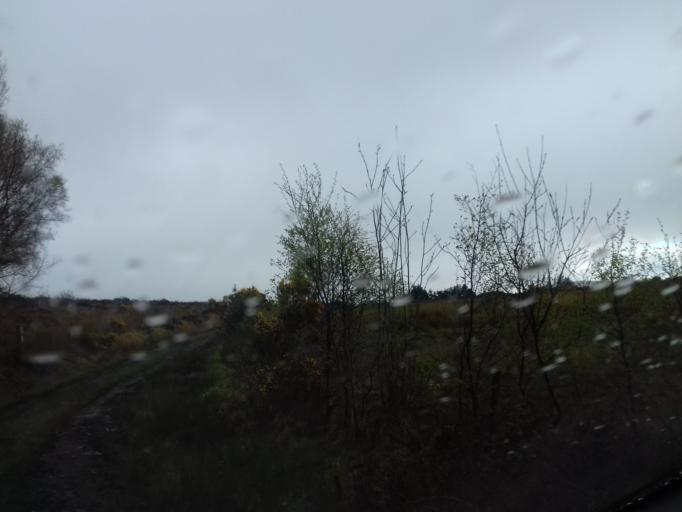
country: IE
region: Connaught
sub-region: County Leitrim
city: Manorhamilton
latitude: 54.2613
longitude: -7.9289
